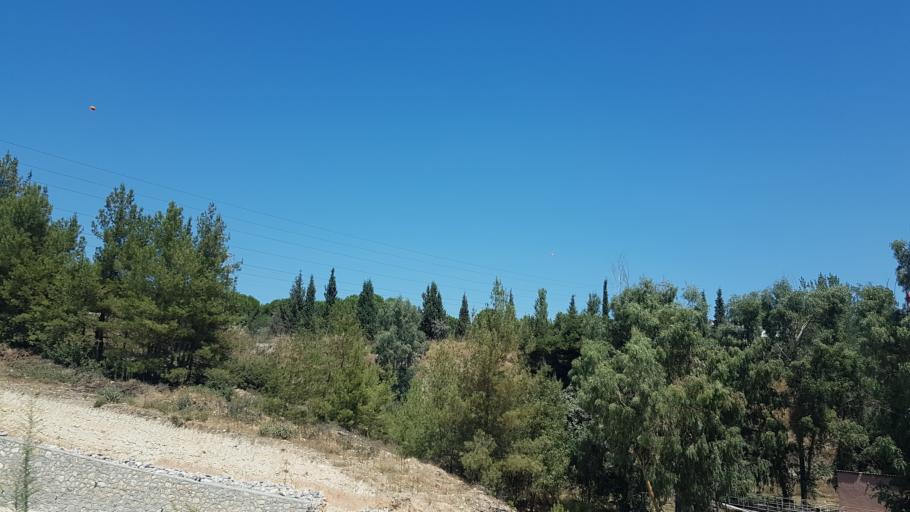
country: TR
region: Mugla
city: Yatagan
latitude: 37.3181
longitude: 28.0844
